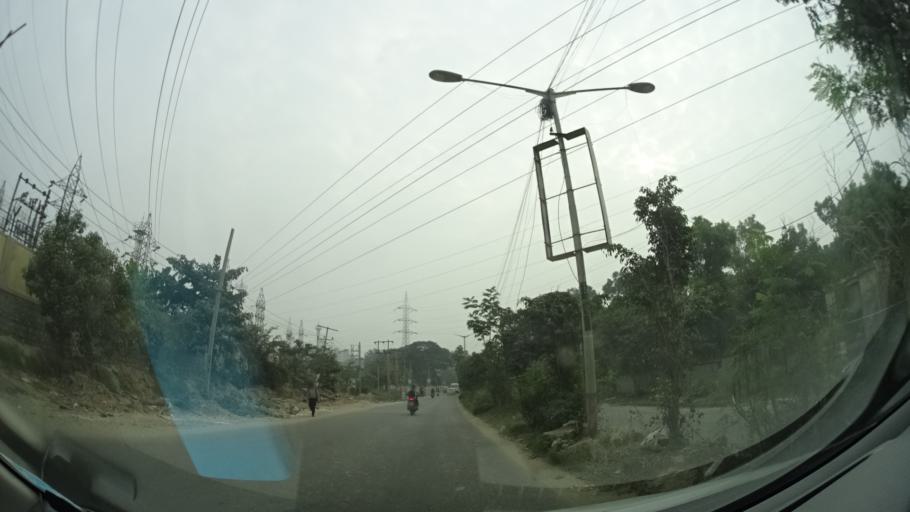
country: IN
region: Karnataka
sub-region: Bangalore Rural
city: Hoskote
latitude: 12.9929
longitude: 77.7096
